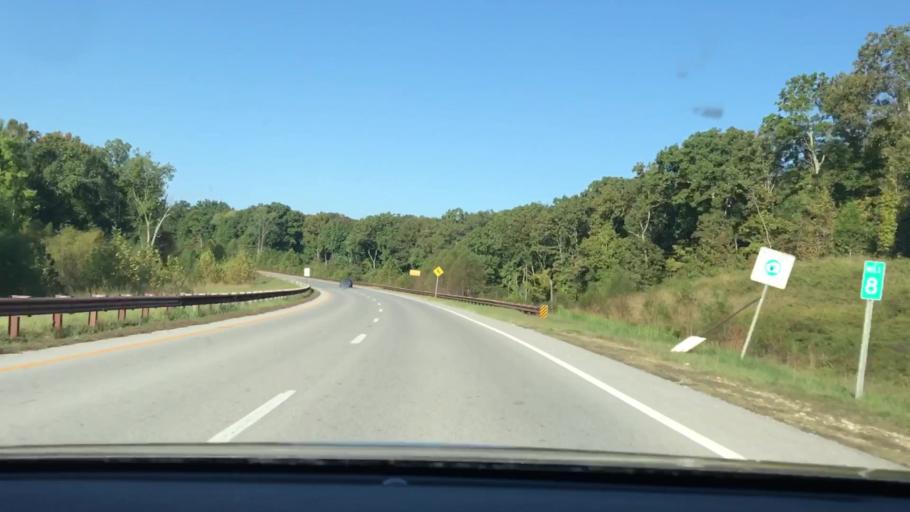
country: US
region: Kentucky
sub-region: Trigg County
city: Cadiz
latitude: 36.8030
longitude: -87.9882
